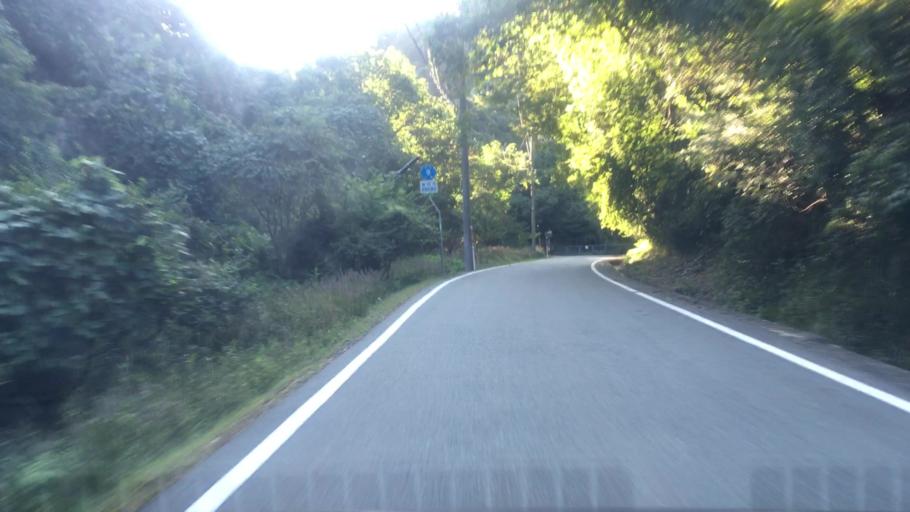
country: JP
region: Hyogo
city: Toyooka
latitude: 35.6109
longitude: 134.8378
